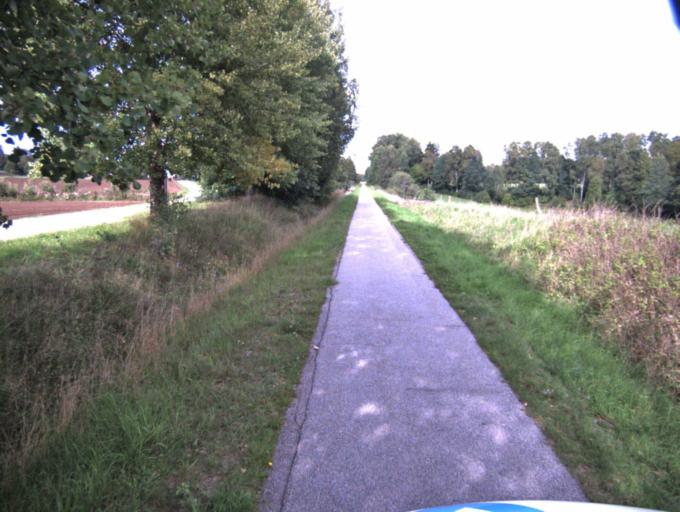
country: SE
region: Vaestra Goetaland
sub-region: Ulricehamns Kommun
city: Ulricehamn
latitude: 57.8478
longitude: 13.4241
